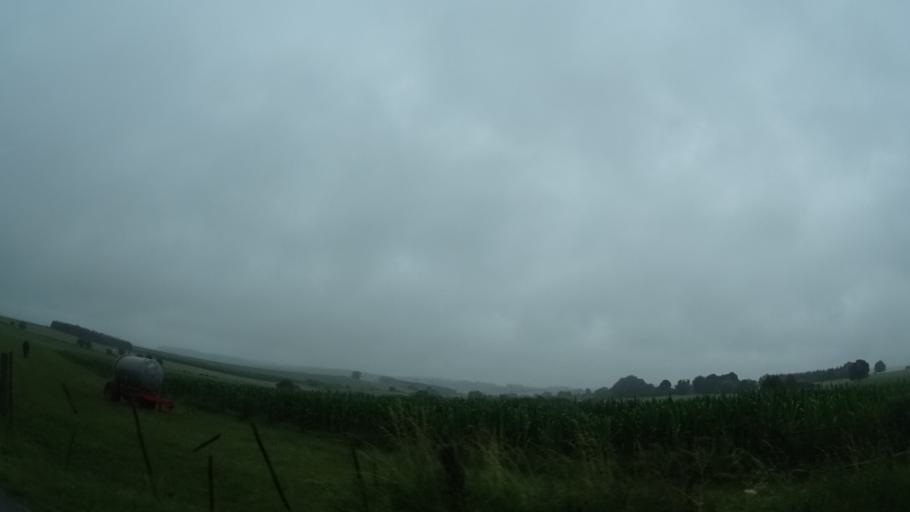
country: BE
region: Wallonia
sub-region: Province du Luxembourg
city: Leglise
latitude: 49.7859
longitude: 5.5396
